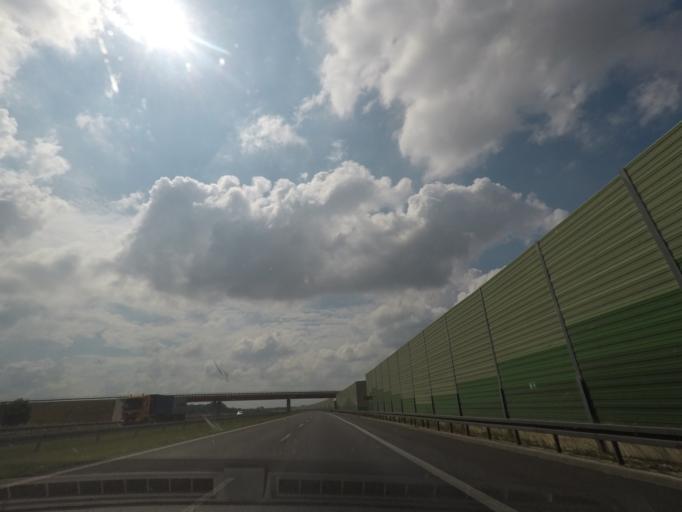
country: PL
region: Lodz Voivodeship
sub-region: Powiat kutnowski
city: Krzyzanow
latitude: 52.1493
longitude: 19.4814
